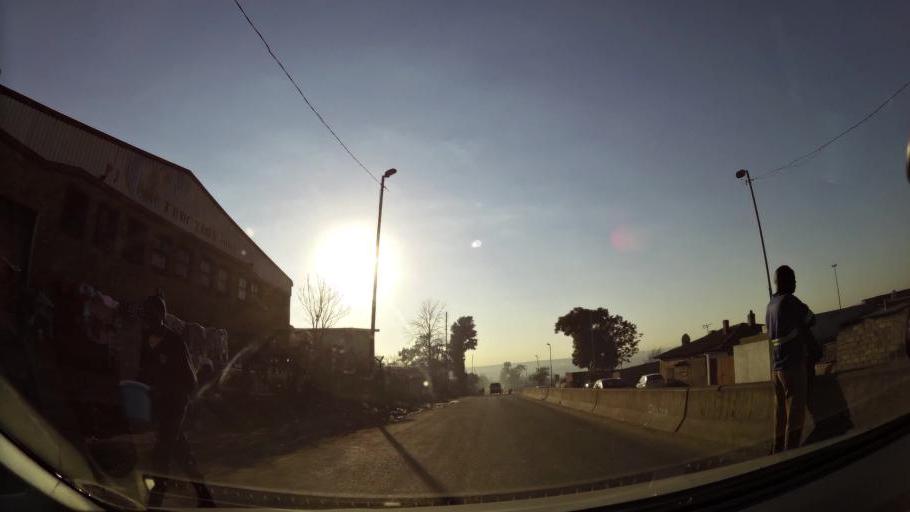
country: ZA
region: Gauteng
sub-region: City of Johannesburg Metropolitan Municipality
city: Modderfontein
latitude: -26.0983
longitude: 28.0950
